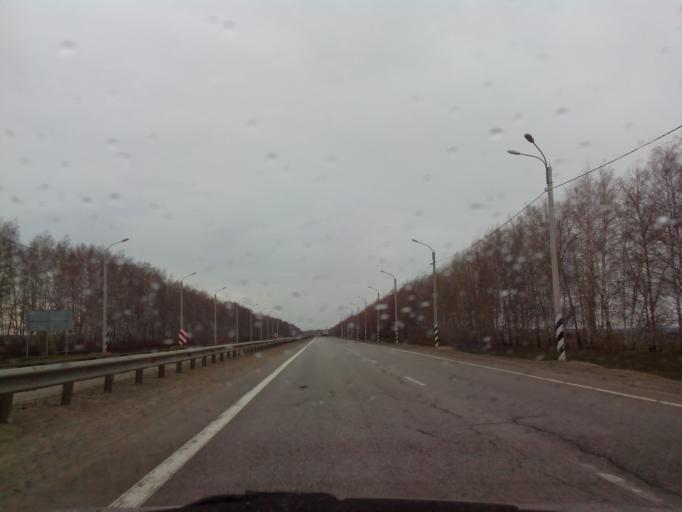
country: RU
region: Tambov
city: Selezni
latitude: 52.7611
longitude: 41.1298
